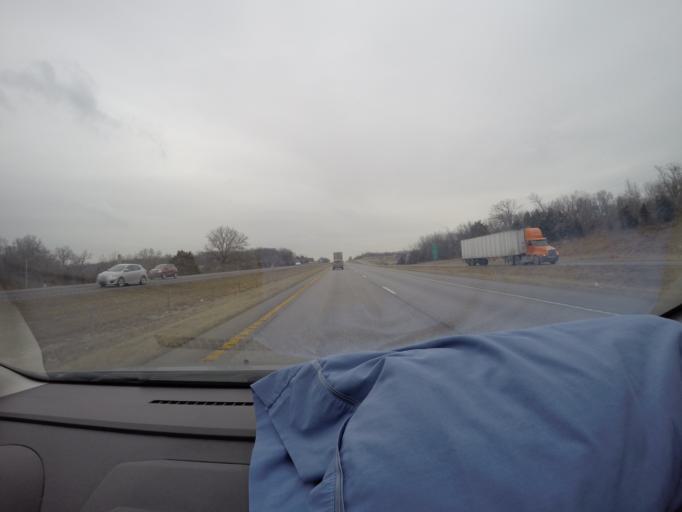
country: US
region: Missouri
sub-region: Warren County
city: Warrenton
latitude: 38.8190
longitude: -91.1068
